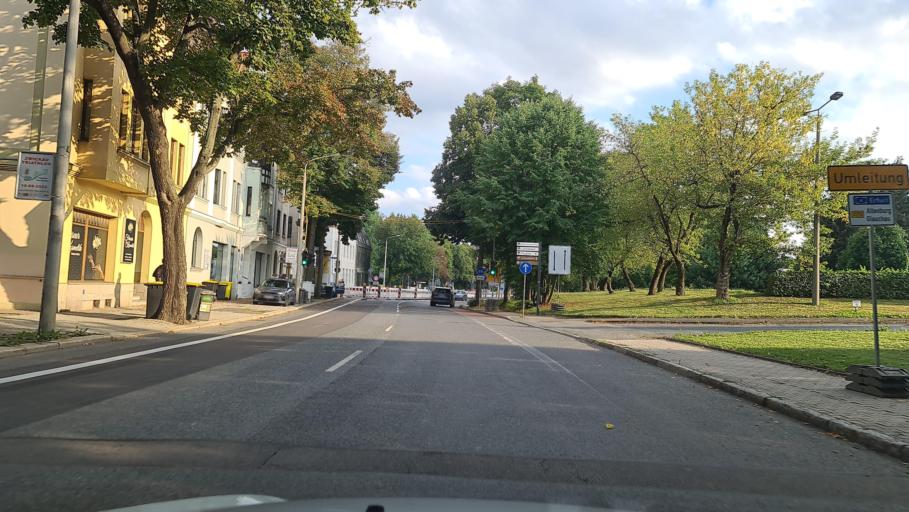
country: DE
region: Saxony
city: Zwickau
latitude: 50.7271
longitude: 12.4849
